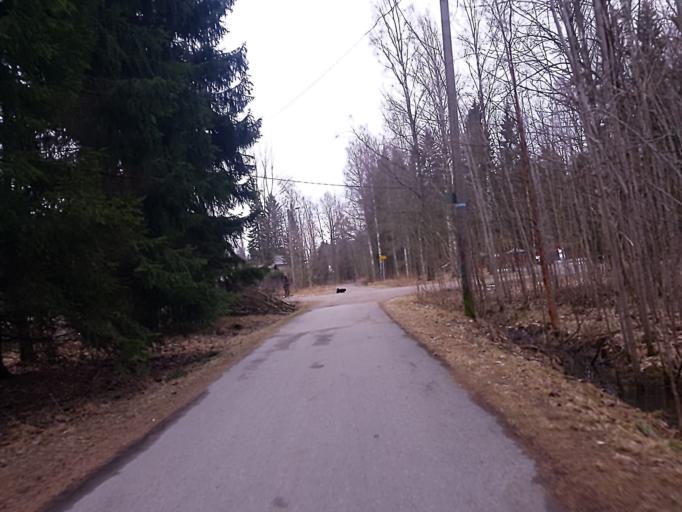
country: FI
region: Uusimaa
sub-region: Helsinki
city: Helsinki
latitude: 60.2379
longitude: 24.9141
